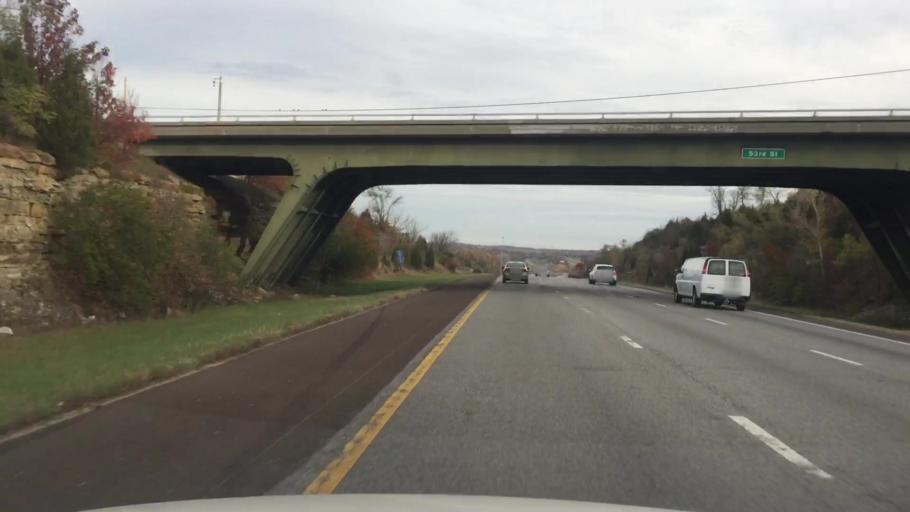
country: US
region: Kansas
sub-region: Wyandotte County
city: Edwardsville
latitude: 39.0325
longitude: -94.7873
